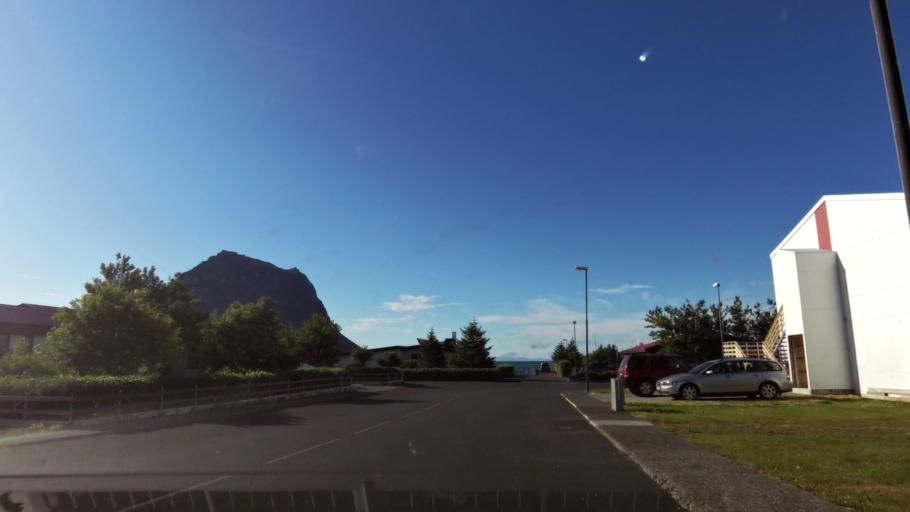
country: IS
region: West
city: Olafsvik
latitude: 64.9252
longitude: -23.2667
